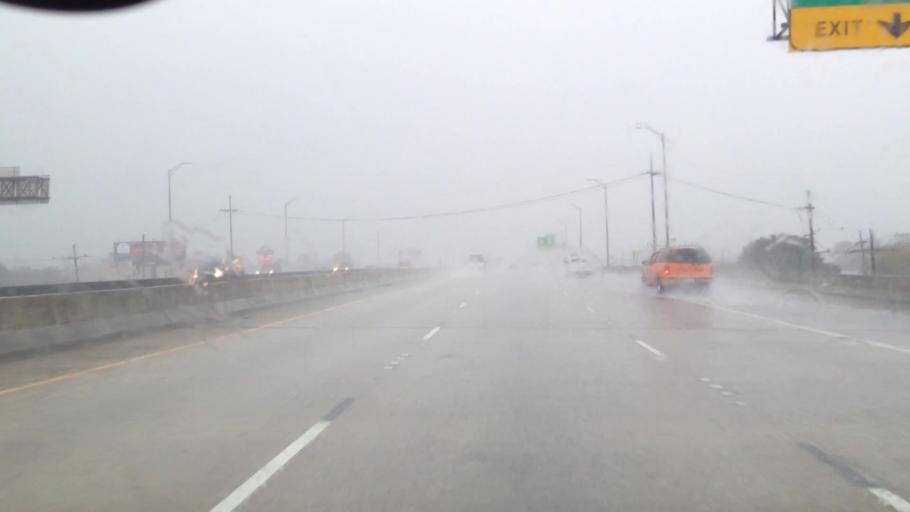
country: US
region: Louisiana
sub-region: Jefferson Parish
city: Gretna
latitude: 29.9133
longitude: -90.0504
